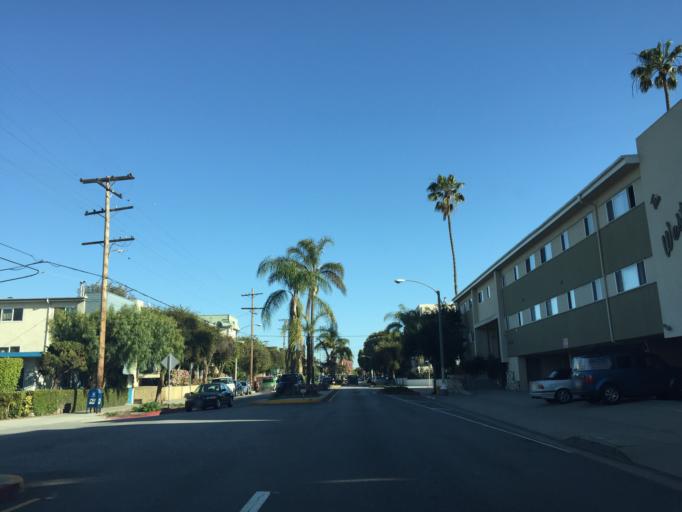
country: US
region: California
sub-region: Los Angeles County
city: Santa Monica
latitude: 34.0077
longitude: -118.4854
